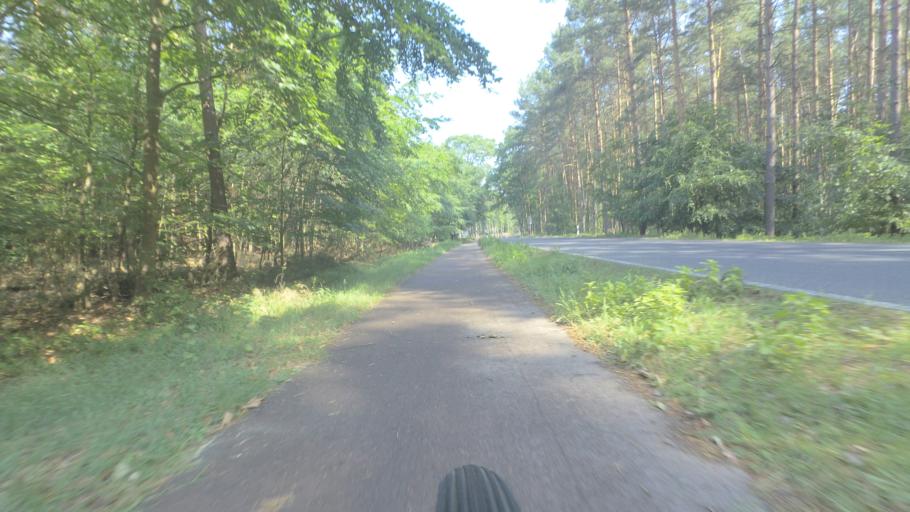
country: DE
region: Saxony-Anhalt
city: Nudersdorf
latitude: 52.0284
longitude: 12.5774
